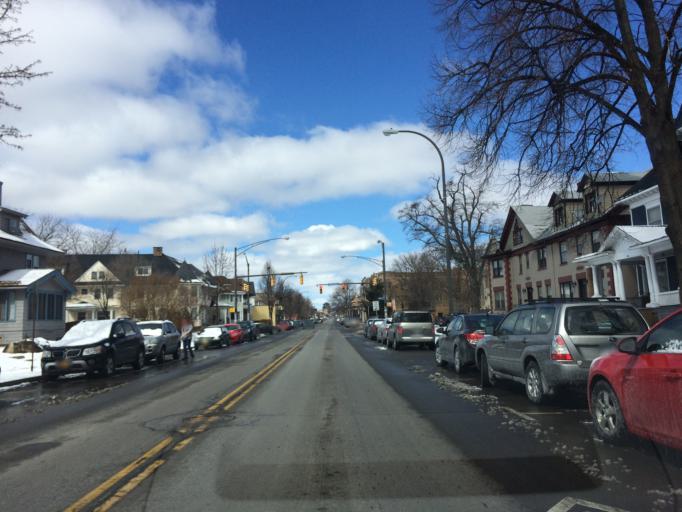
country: US
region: New York
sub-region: Monroe County
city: Brighton
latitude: 43.1396
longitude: -77.5813
